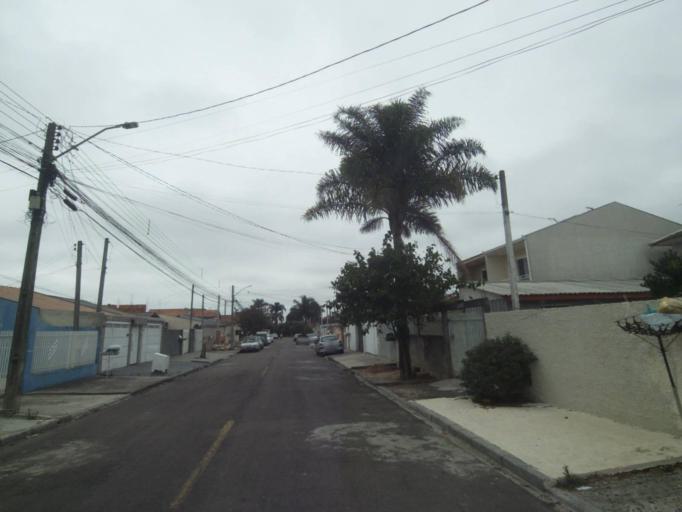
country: BR
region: Parana
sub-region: Araucaria
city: Araucaria
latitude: -25.5468
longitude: -49.3439
